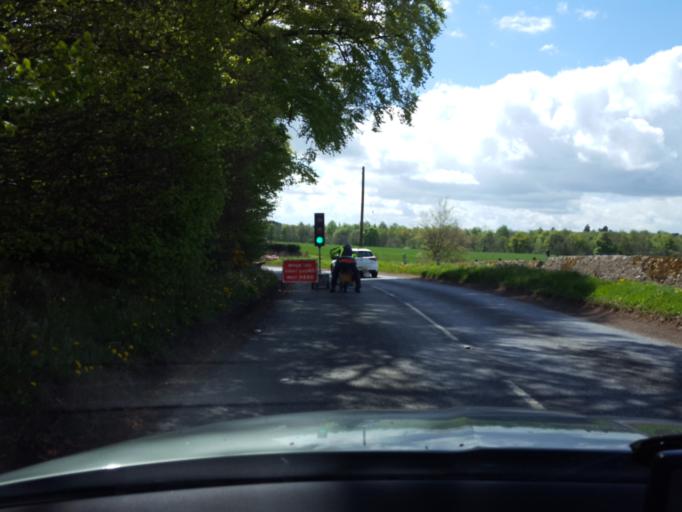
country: GB
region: Scotland
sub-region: Angus
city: Brechin
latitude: 56.7889
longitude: -2.6477
